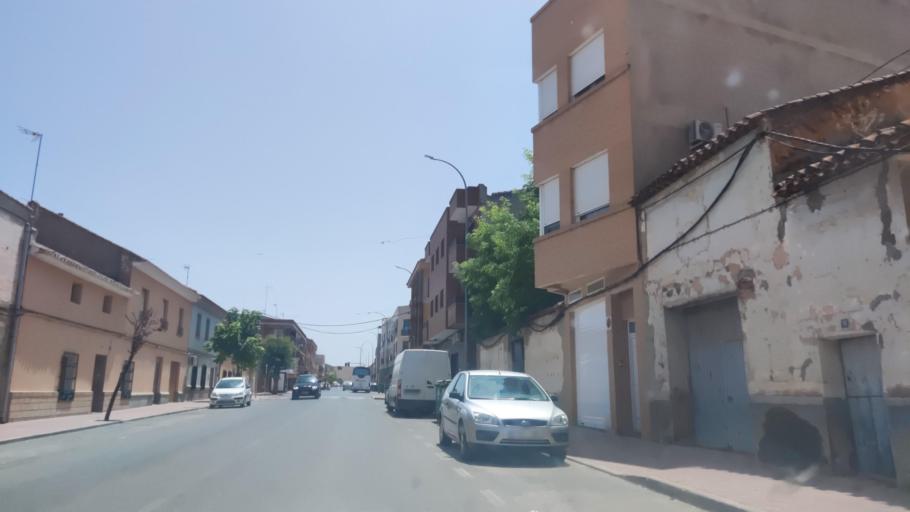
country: ES
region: Castille-La Mancha
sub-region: Provincia de Albacete
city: Pozo-Canada
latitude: 38.8045
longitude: -1.7332
